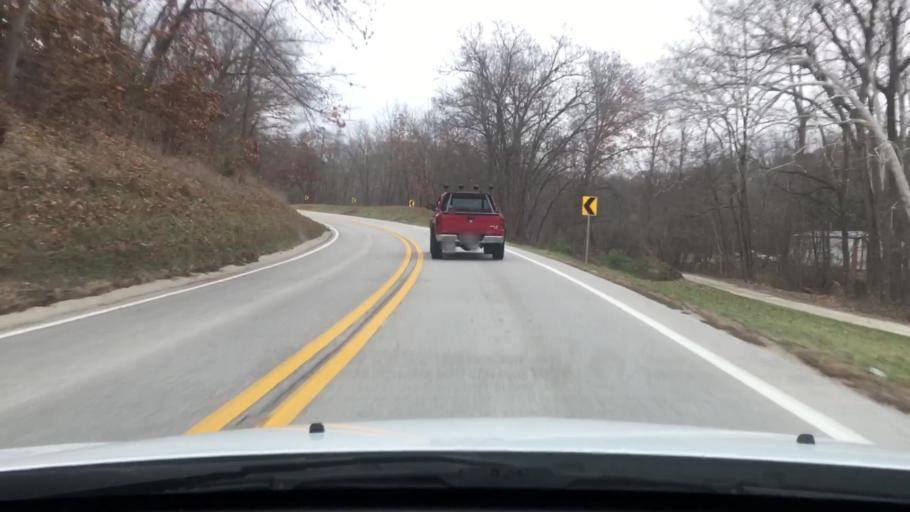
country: US
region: Missouri
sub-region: Pike County
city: Louisiana
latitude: 39.5191
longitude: -90.9506
